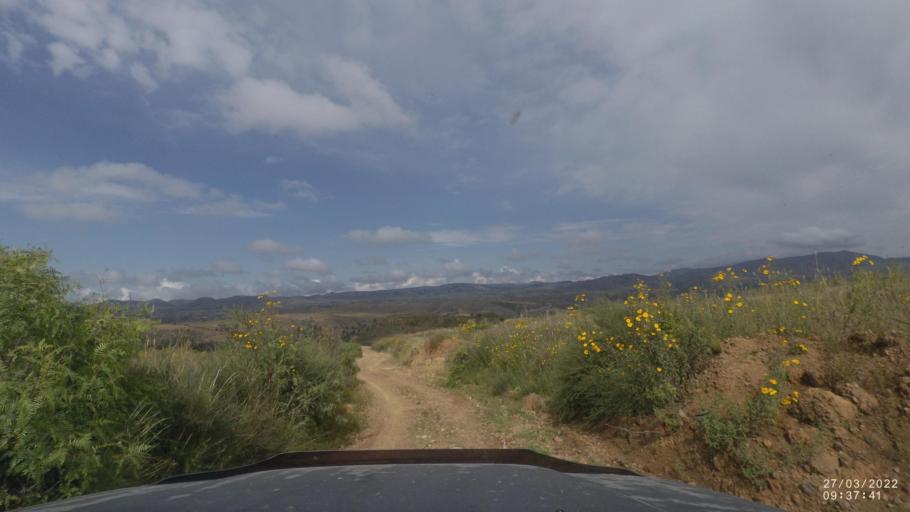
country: BO
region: Cochabamba
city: Cliza
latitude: -17.7460
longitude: -65.8932
